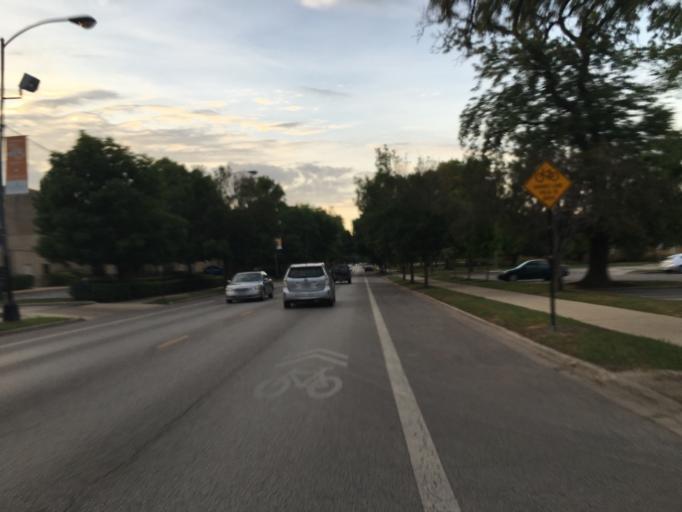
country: US
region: Illinois
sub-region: Cook County
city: Lincolnwood
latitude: 41.9505
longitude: -87.6981
